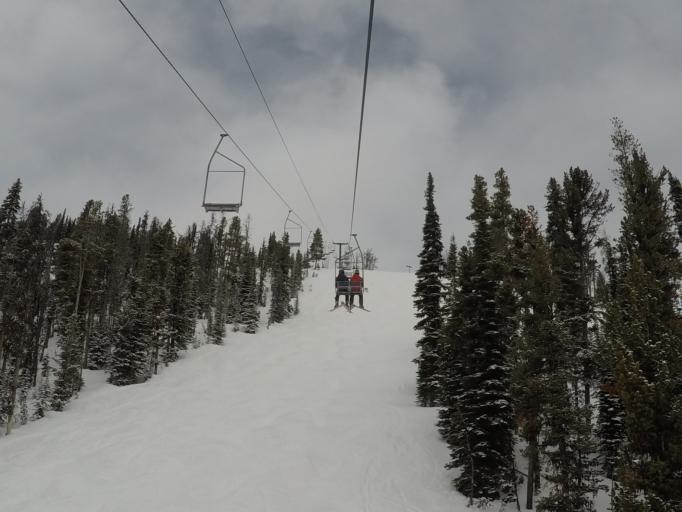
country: US
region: Montana
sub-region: Meagher County
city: White Sulphur Springs
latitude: 46.8363
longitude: -110.7140
